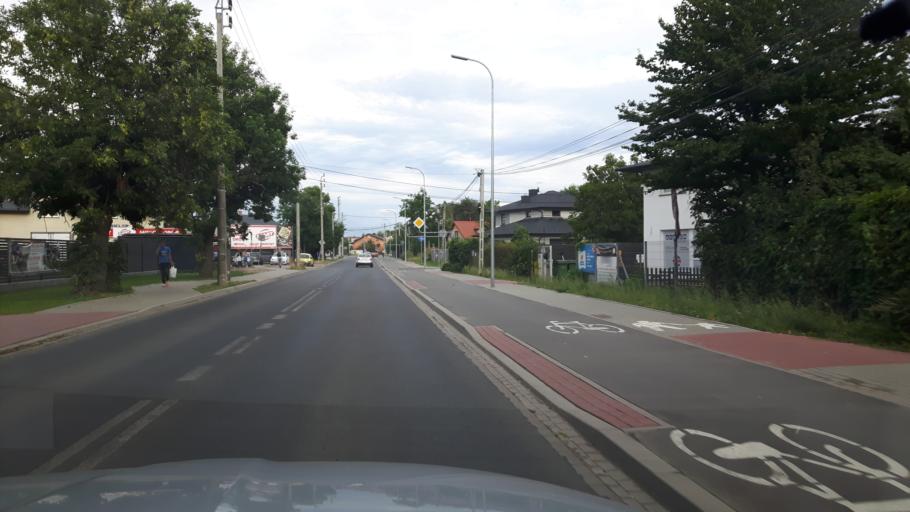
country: PL
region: Masovian Voivodeship
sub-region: Powiat wolominski
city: Marki
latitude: 52.3209
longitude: 21.0906
